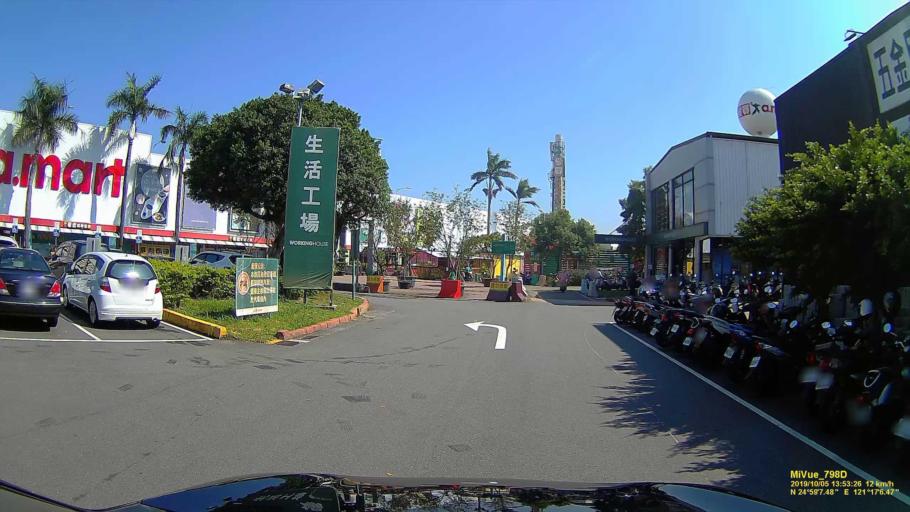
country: TW
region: Taiwan
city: Taoyuan City
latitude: 24.9854
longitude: 121.2852
